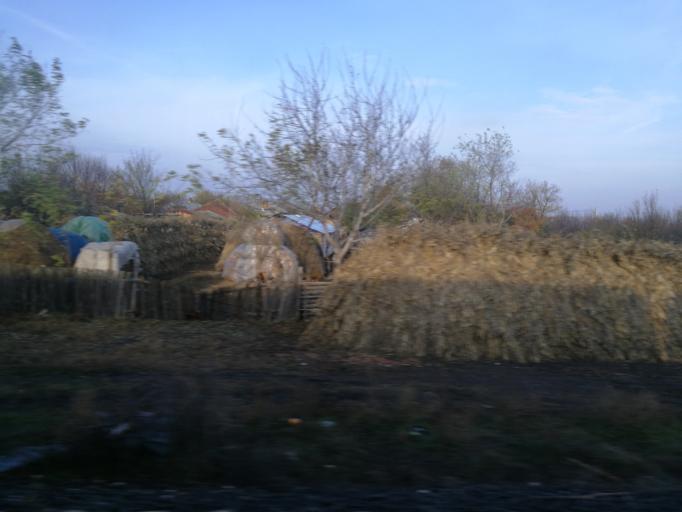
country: RO
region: Buzau
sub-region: Comuna Cochirleanca
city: Cochirleanca
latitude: 45.2768
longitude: 27.0066
